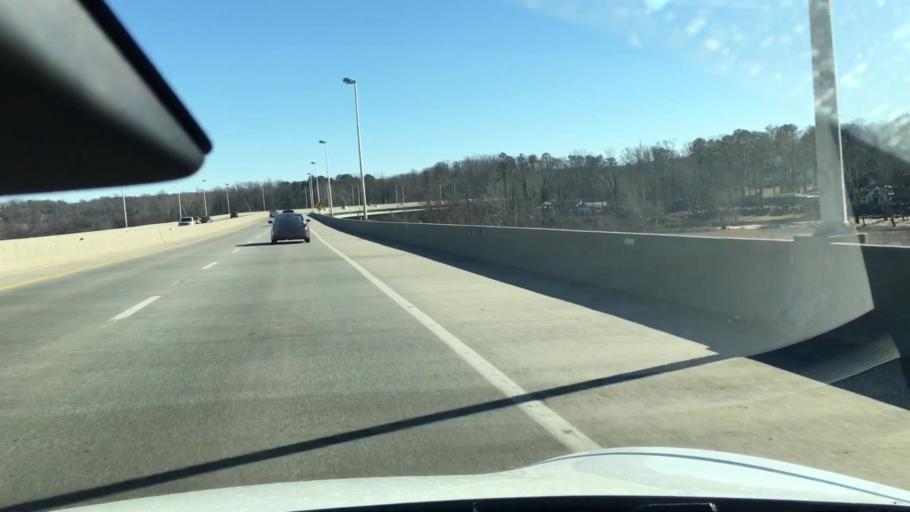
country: US
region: Virginia
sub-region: Henrico County
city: Tuckahoe
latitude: 37.5612
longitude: -77.5739
